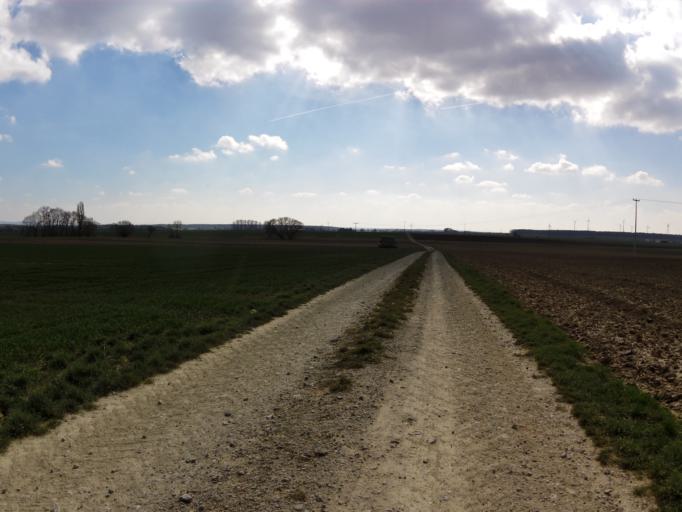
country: DE
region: Bavaria
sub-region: Regierungsbezirk Unterfranken
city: Biebelried
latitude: 49.7518
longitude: 10.0809
